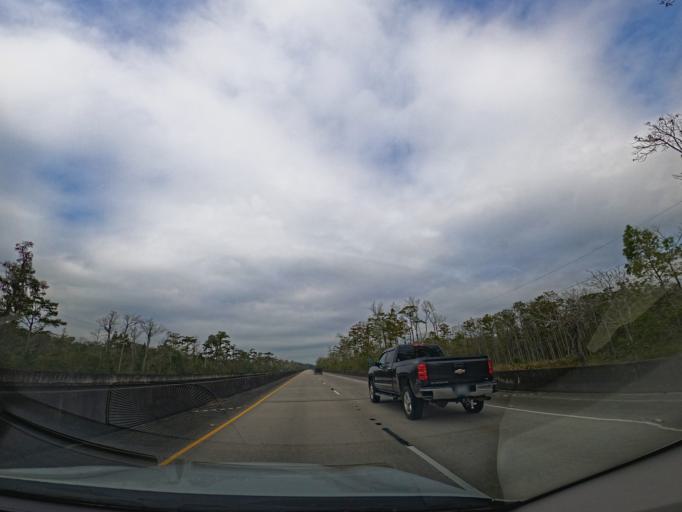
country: US
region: Louisiana
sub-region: Saint Mary Parish
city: Amelia
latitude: 29.6686
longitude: -91.0704
